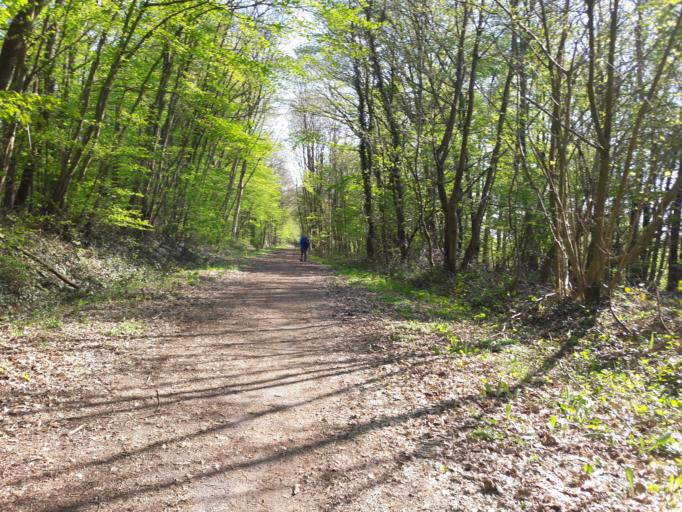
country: FR
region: Nord-Pas-de-Calais
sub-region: Departement du Nord
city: Sains-du-Nord
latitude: 50.1465
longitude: 4.0683
